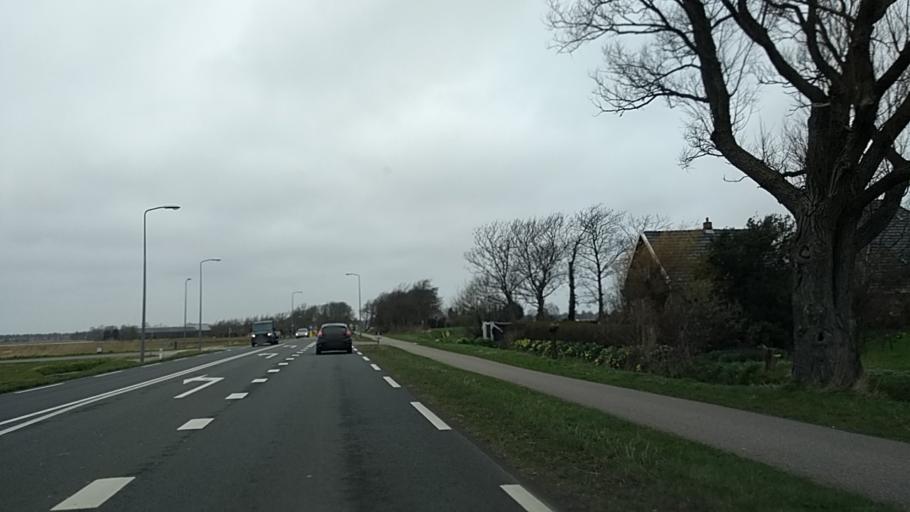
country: NL
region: North Holland
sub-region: Gemeente Alkmaar
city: Alkmaar
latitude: 52.6510
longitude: 4.7216
